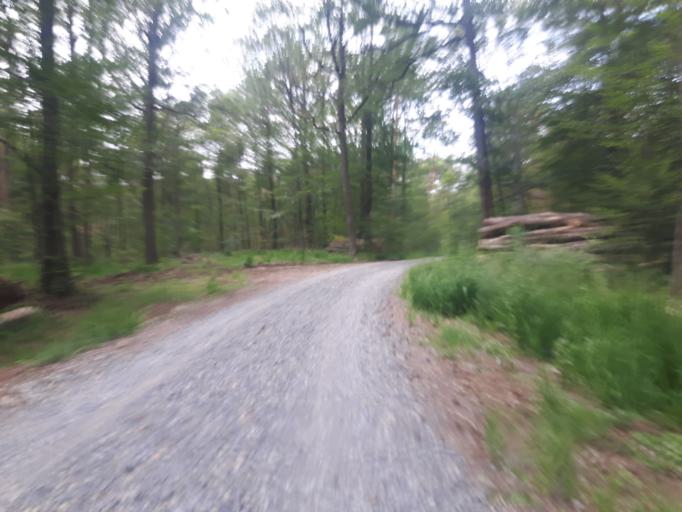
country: DE
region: Baden-Wuerttemberg
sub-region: Regierungsbezirk Stuttgart
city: Cleebronn
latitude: 49.0307
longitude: 9.0176
